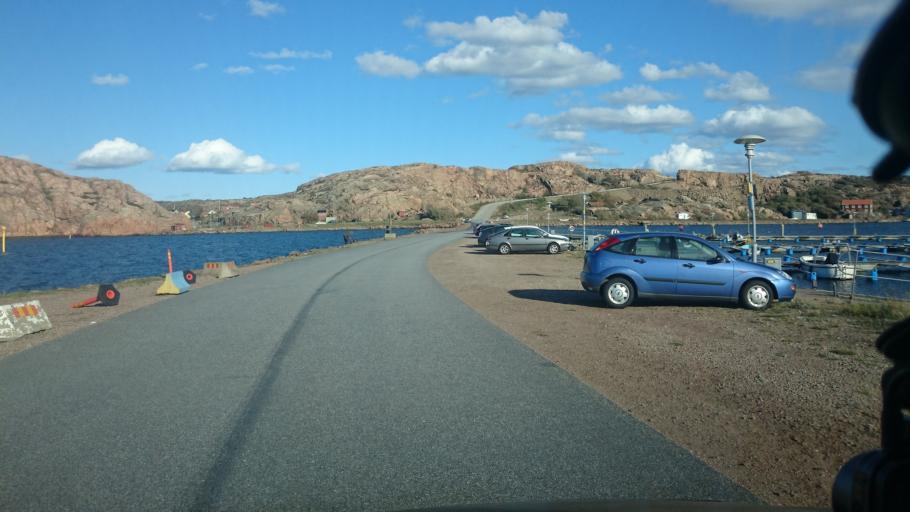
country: SE
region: Vaestra Goetaland
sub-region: Lysekils Kommun
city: Lysekil
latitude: 58.3172
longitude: 11.3963
